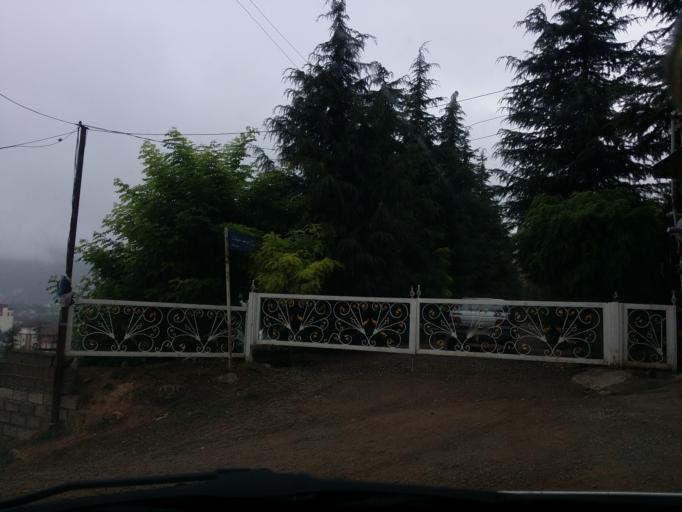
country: IR
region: Mazandaran
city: `Abbasabad
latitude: 36.5096
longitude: 51.1538
